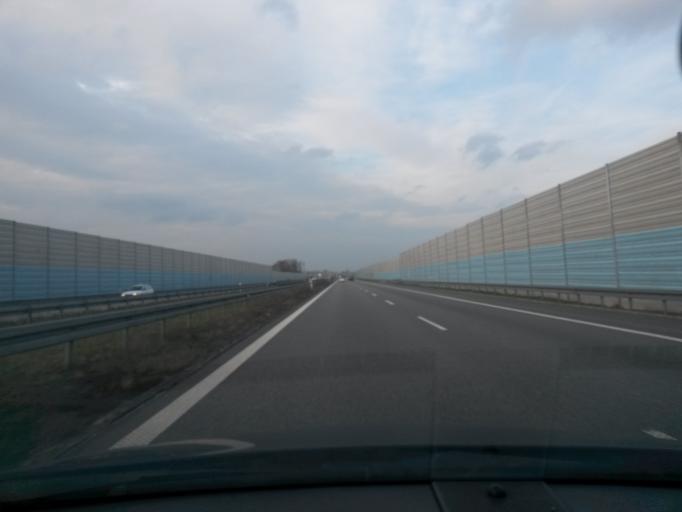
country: PL
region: Lodz Voivodeship
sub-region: powiat Lowicki
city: Lyszkowice
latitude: 51.9787
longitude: 19.8812
